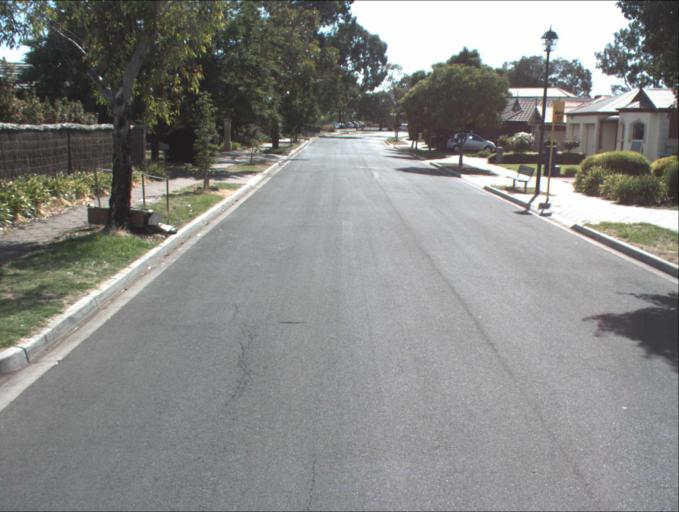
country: AU
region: South Australia
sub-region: Port Adelaide Enfield
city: Gilles Plains
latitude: -34.8613
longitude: 138.6550
